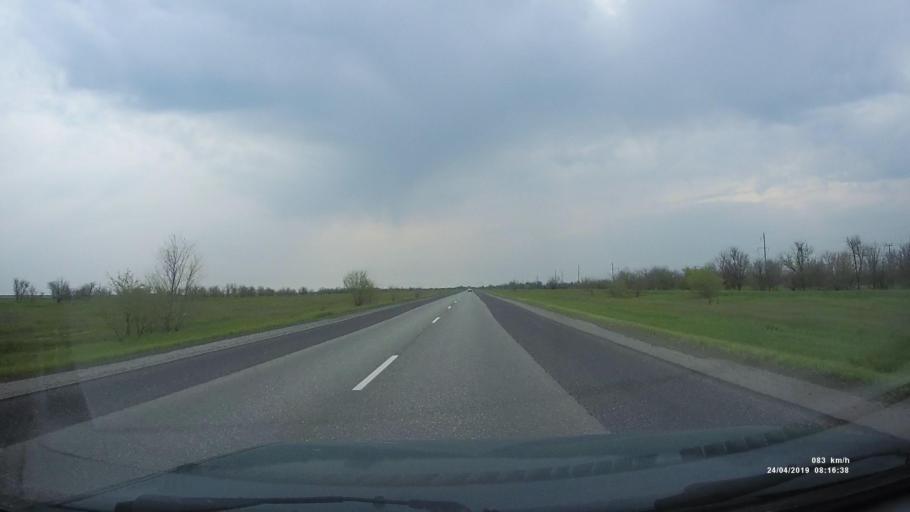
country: RU
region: Kalmykiya
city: Priyutnoye
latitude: 46.0987
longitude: 43.6159
